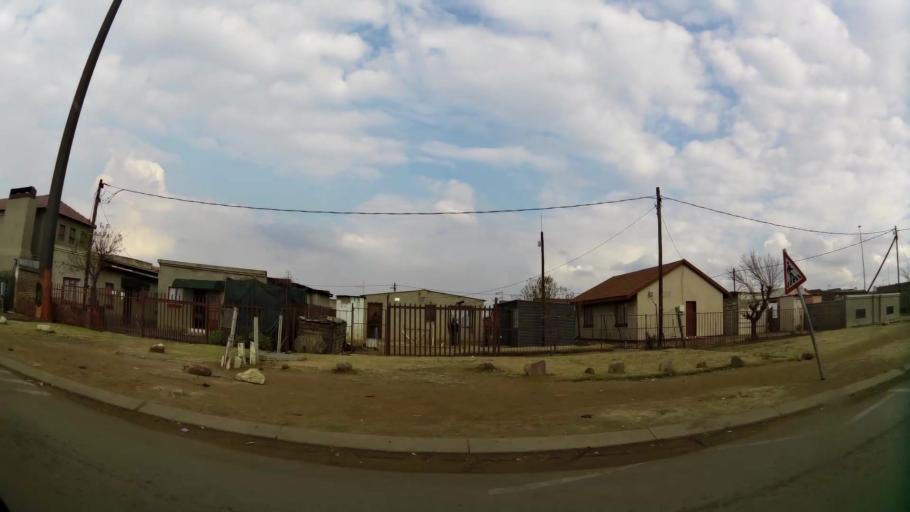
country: ZA
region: Gauteng
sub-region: Sedibeng District Municipality
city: Vereeniging
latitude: -26.6730
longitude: 27.8756
